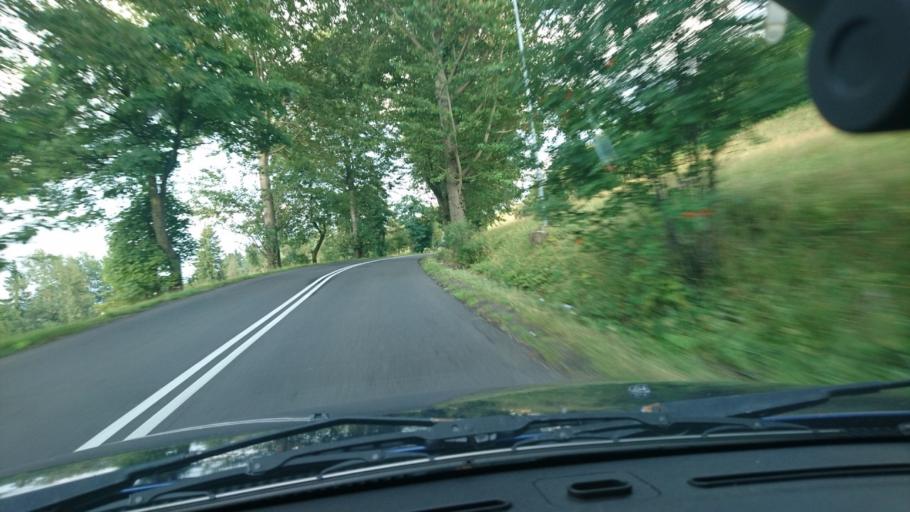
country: PL
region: Silesian Voivodeship
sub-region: Powiat cieszynski
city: Koniakow
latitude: 49.5478
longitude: 18.9564
